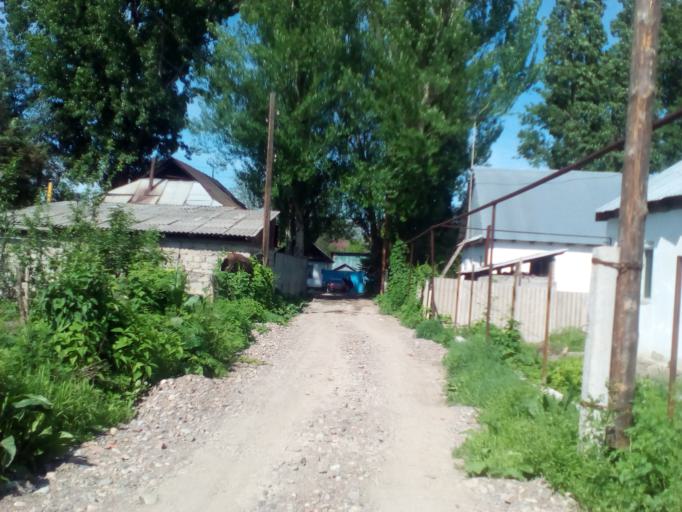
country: KZ
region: Almaty Oblysy
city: Burunday
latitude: 43.2234
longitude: 76.3170
